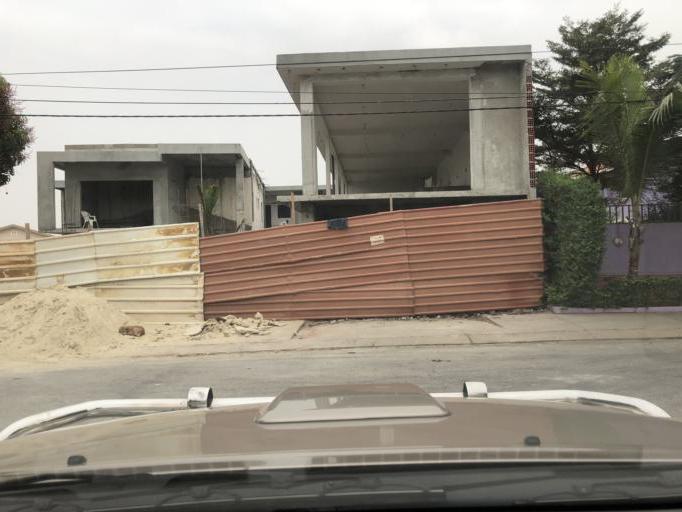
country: AO
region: Luanda
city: Luanda
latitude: -8.9073
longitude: 13.2245
